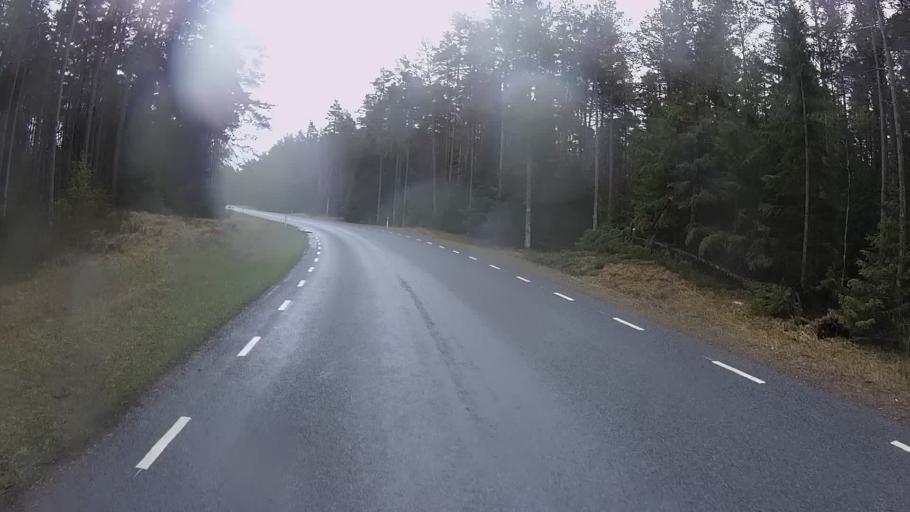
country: EE
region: Hiiumaa
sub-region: Kaerdla linn
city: Kardla
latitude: 58.9123
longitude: 22.3872
